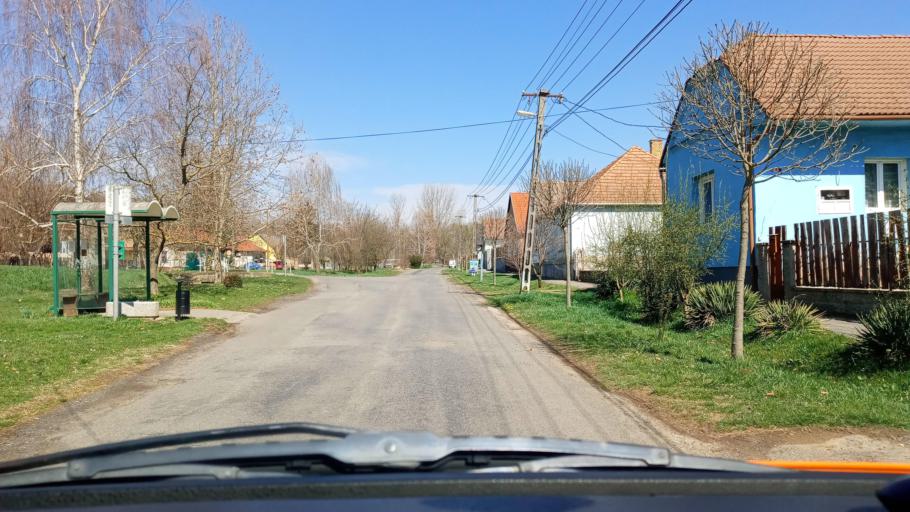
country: HU
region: Baranya
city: Pecsvarad
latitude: 46.0674
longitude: 18.4491
